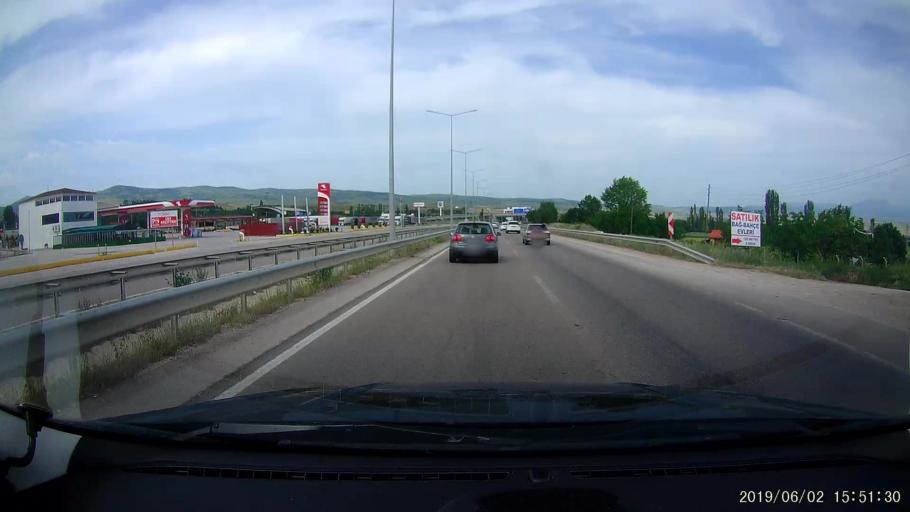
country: TR
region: Amasya
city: Merzifon
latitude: 40.8680
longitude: 35.4960
